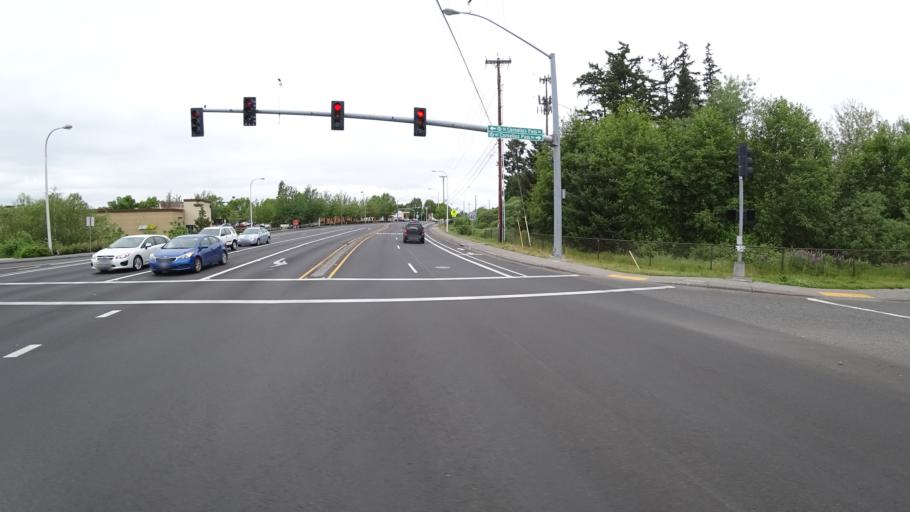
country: US
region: Oregon
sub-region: Washington County
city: Aloha
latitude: 45.5154
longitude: -122.9011
